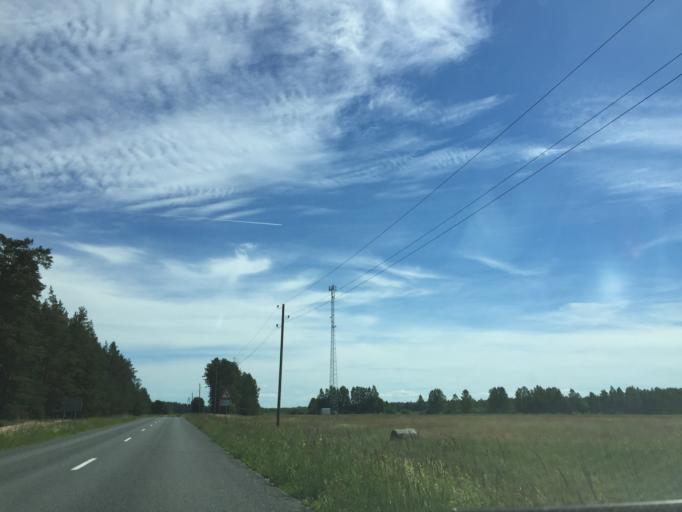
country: LV
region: Dundaga
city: Dundaga
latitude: 57.6312
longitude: 22.5706
